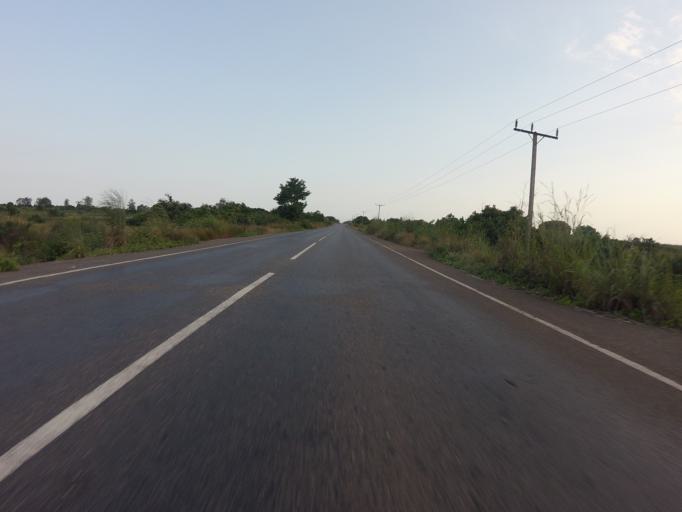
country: GH
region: Volta
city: Anloga
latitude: 6.0684
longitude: 0.6045
